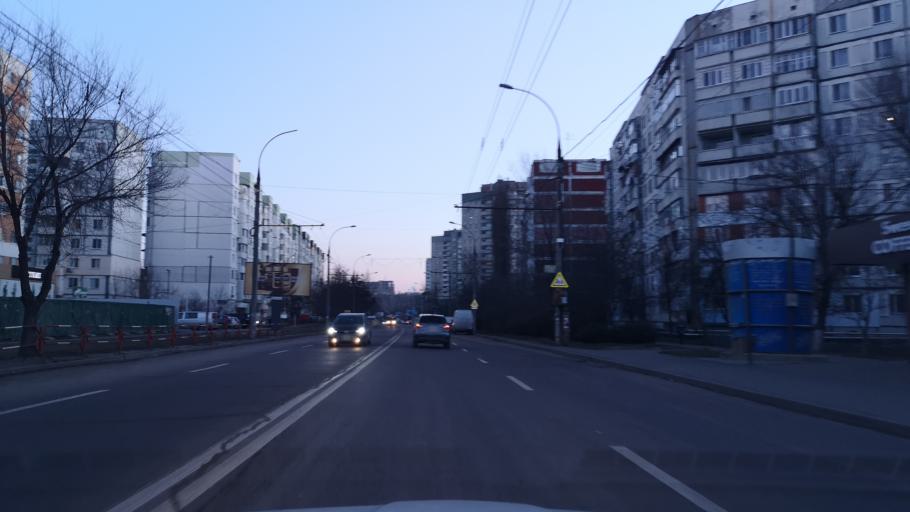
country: MD
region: Chisinau
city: Stauceni
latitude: 47.0576
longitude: 28.8479
